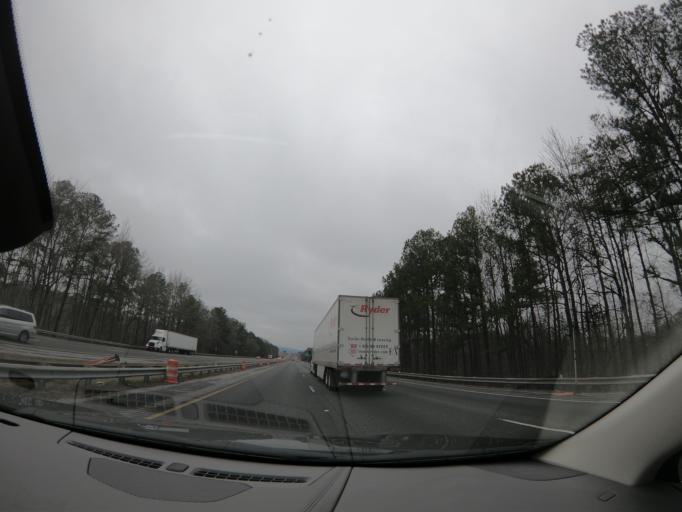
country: US
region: Georgia
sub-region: Whitfield County
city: Dalton
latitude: 34.6424
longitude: -84.9795
